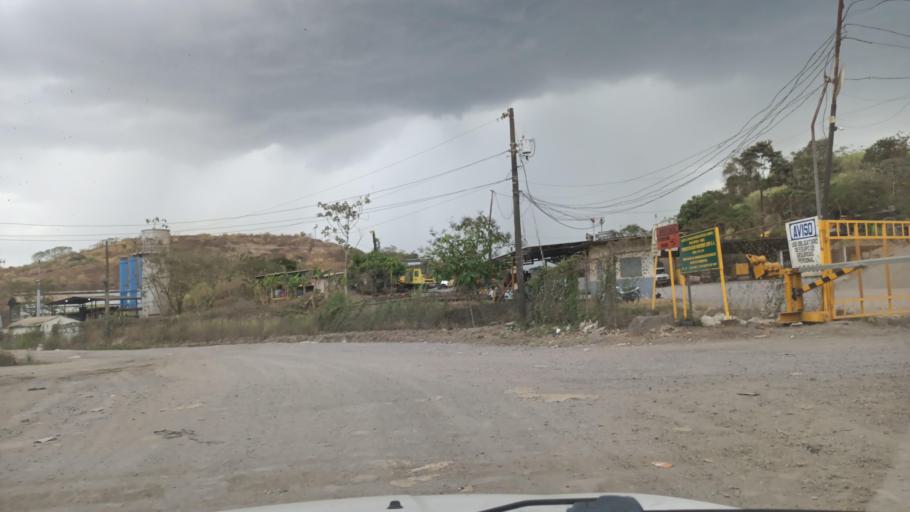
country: PA
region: Panama
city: Las Cumbres
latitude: 9.0537
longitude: -79.5691
